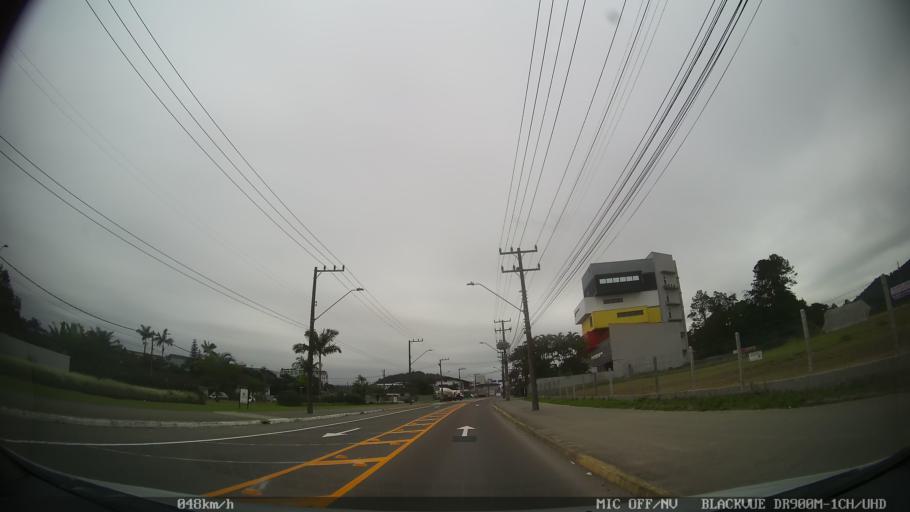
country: BR
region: Santa Catarina
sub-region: Joinville
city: Joinville
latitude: -26.2566
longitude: -48.8516
